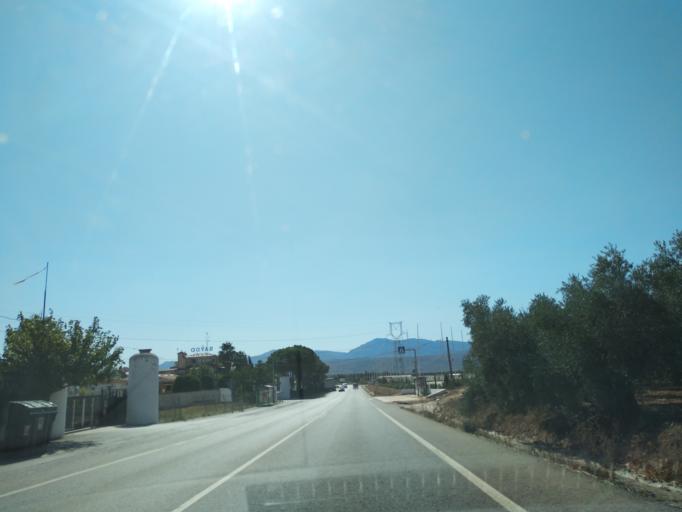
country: ES
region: Andalusia
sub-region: Provincia de Malaga
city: Mollina
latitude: 37.1022
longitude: -4.6356
